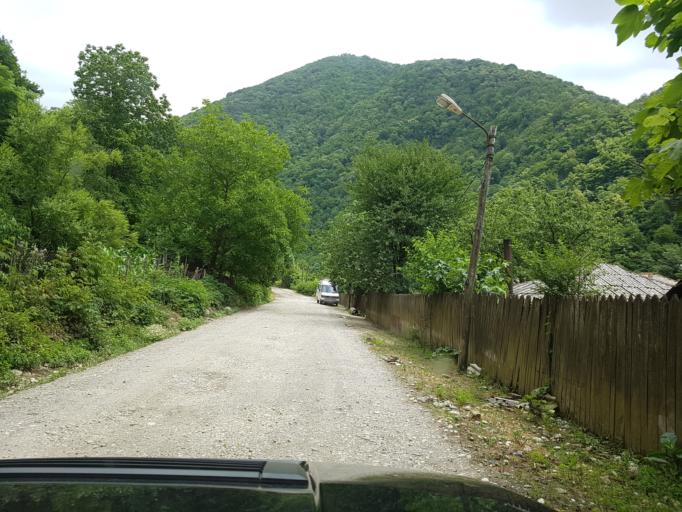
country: GE
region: Imereti
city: Kutaisi
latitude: 42.4374
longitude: 42.7526
